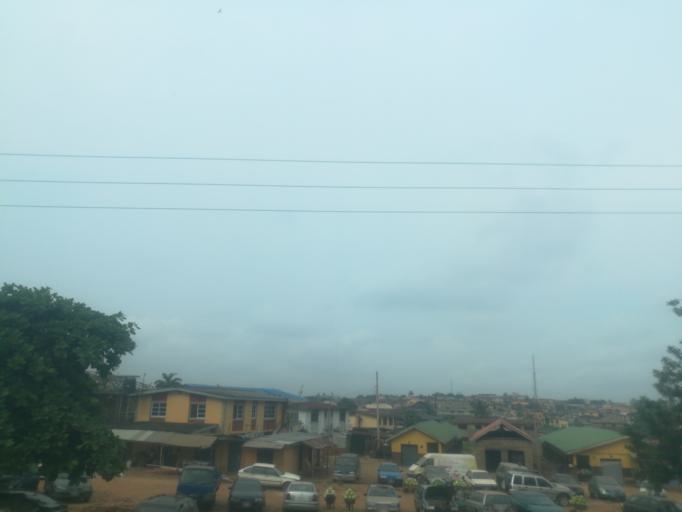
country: NG
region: Oyo
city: Ibadan
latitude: 7.4110
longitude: 3.9431
